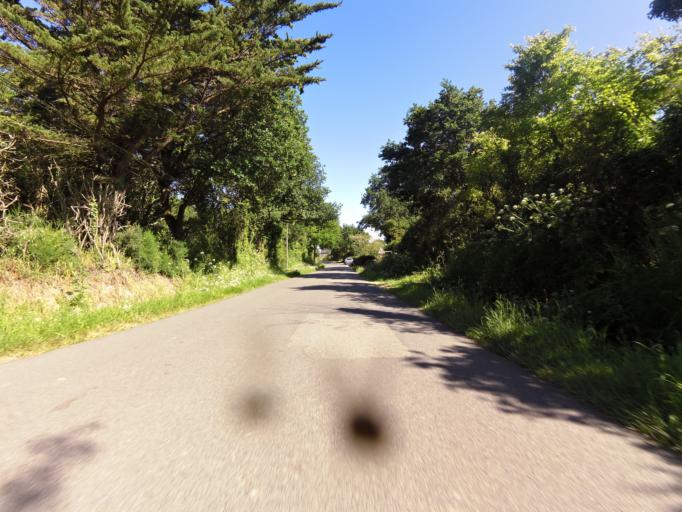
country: FR
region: Brittany
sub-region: Departement du Morbihan
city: Penestin
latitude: 47.4711
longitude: -2.4589
